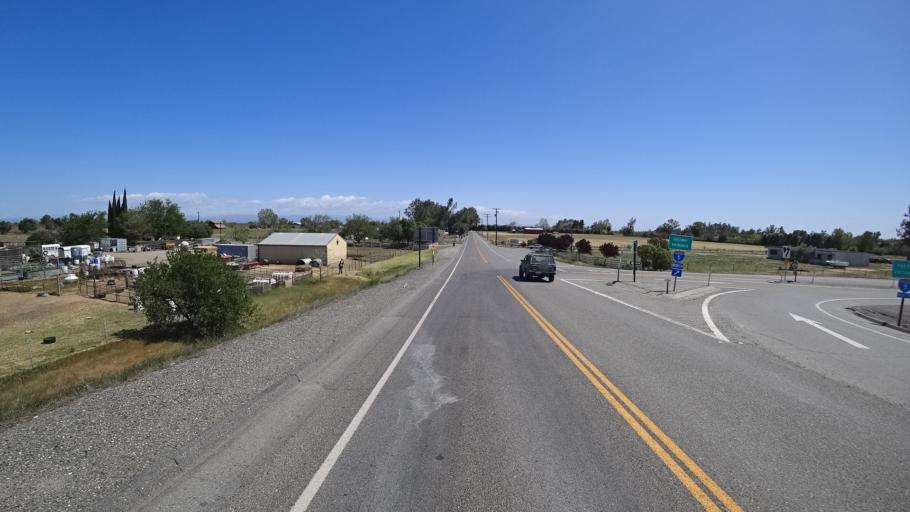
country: US
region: California
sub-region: Glenn County
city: Orland
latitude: 39.7838
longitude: -122.2029
